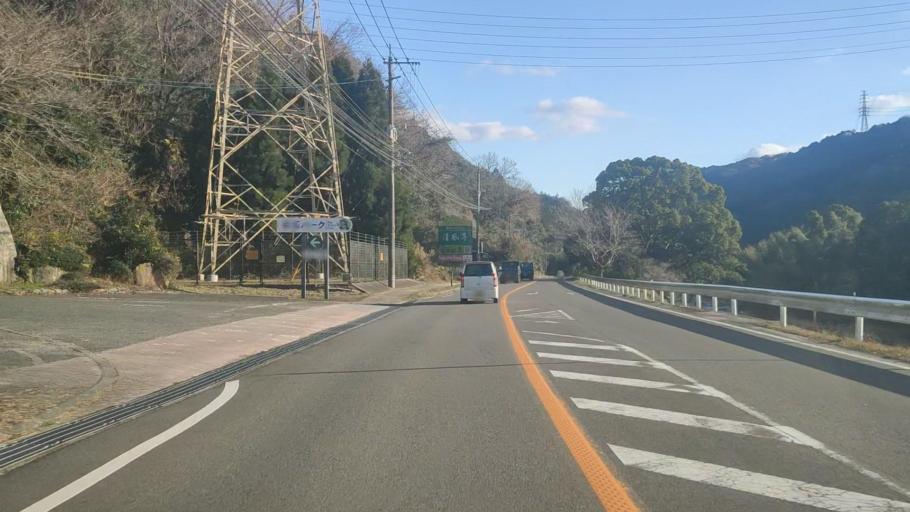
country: JP
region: Saga Prefecture
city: Saga-shi
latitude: 33.3367
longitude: 130.2608
